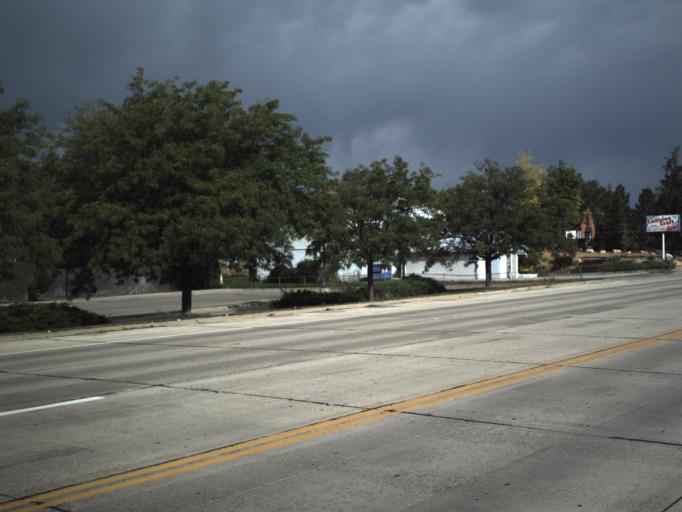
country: US
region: Utah
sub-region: Weber County
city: Harrisville
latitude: 41.2634
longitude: -111.9695
